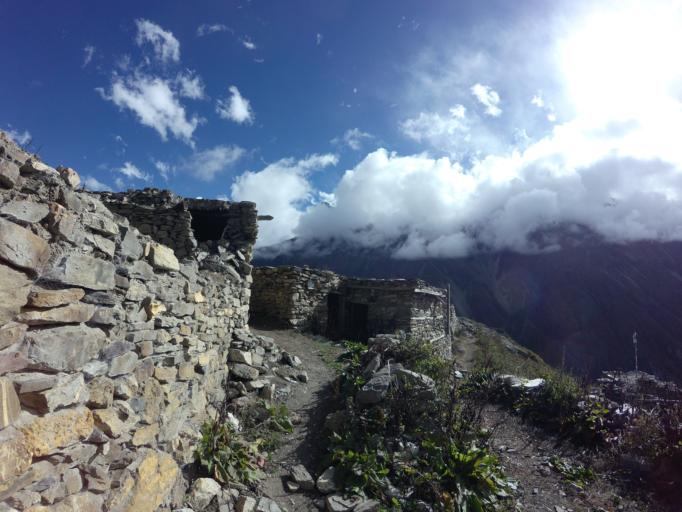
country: NP
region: Western Region
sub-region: Gandaki Zone
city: Nawal
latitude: 28.6767
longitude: 83.9719
